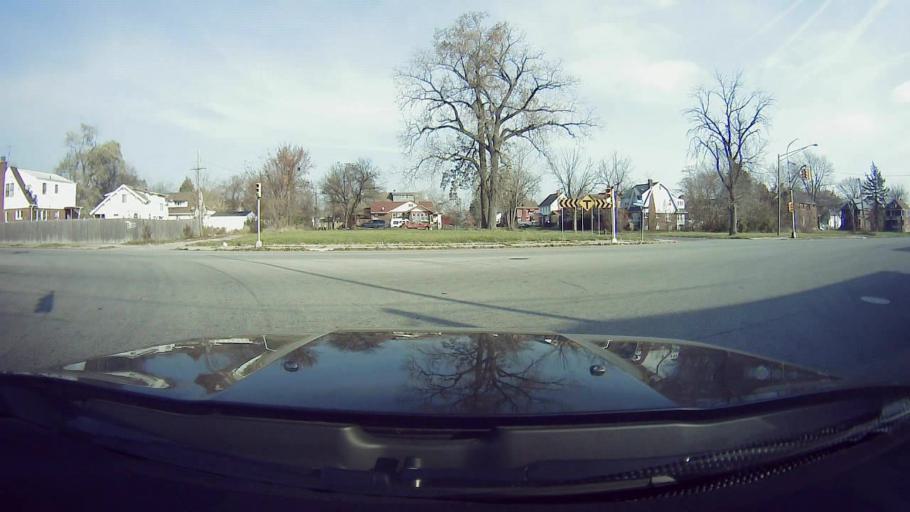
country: US
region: Michigan
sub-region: Wayne County
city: Highland Park
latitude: 42.4105
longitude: -83.1118
